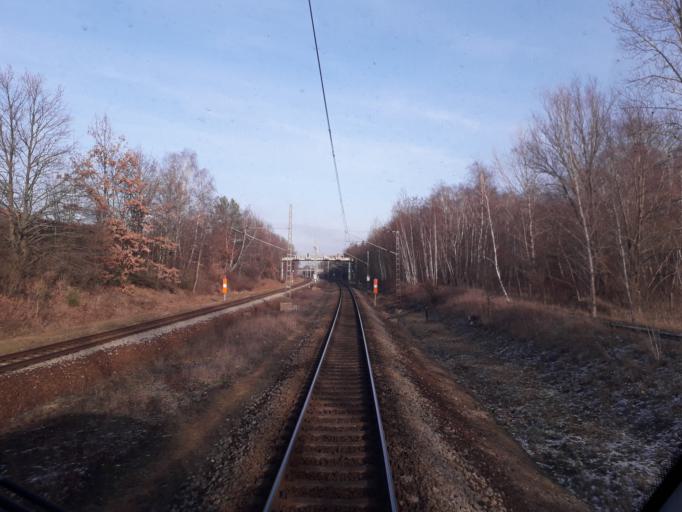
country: DE
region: Berlin
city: Altglienicke
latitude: 52.4099
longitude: 13.5491
